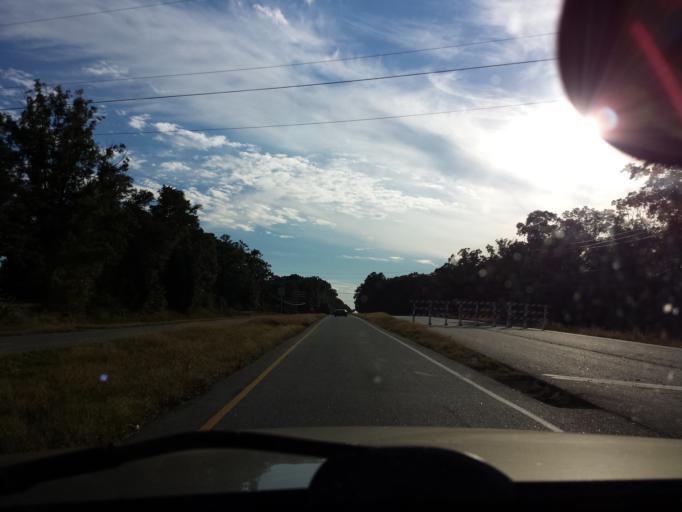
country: US
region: Georgia
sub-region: Bartow County
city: Cartersville
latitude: 34.1269
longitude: -84.8553
